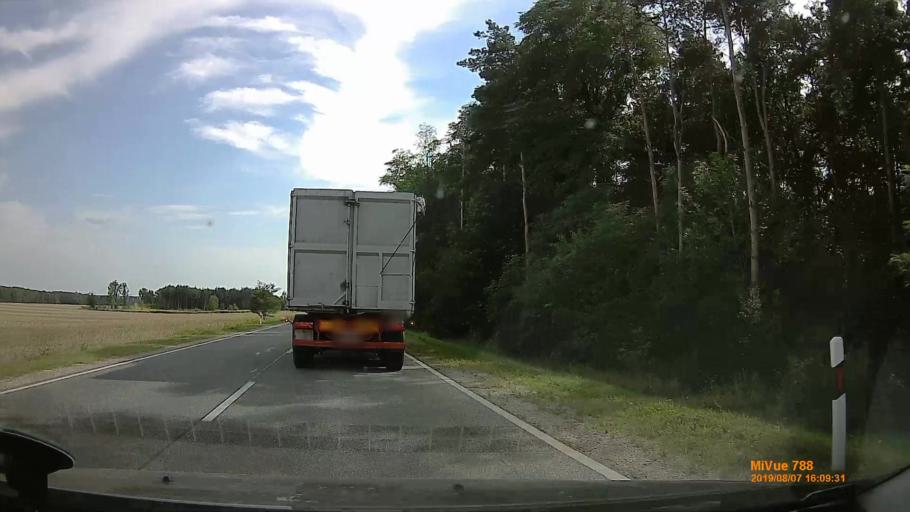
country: HU
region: Zala
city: Zalalovo
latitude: 46.8921
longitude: 16.6020
